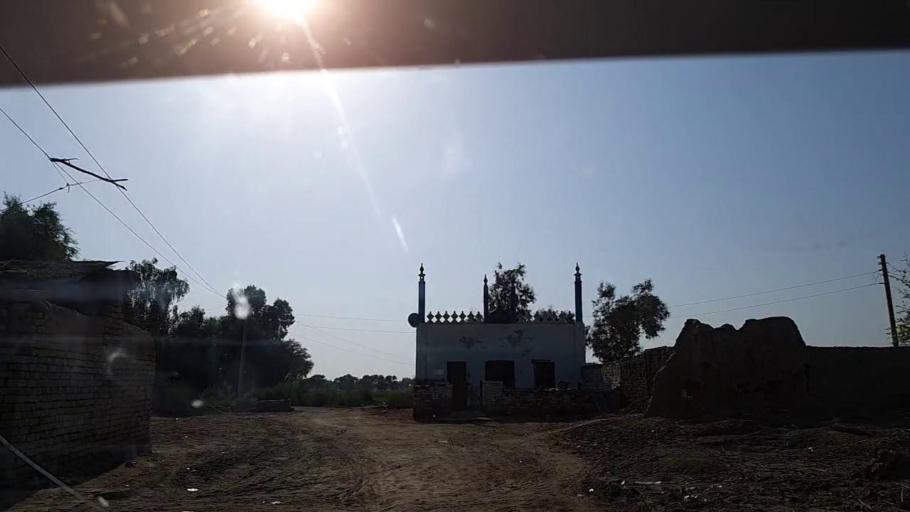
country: PK
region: Sindh
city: Tangwani
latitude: 28.2393
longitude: 68.9907
